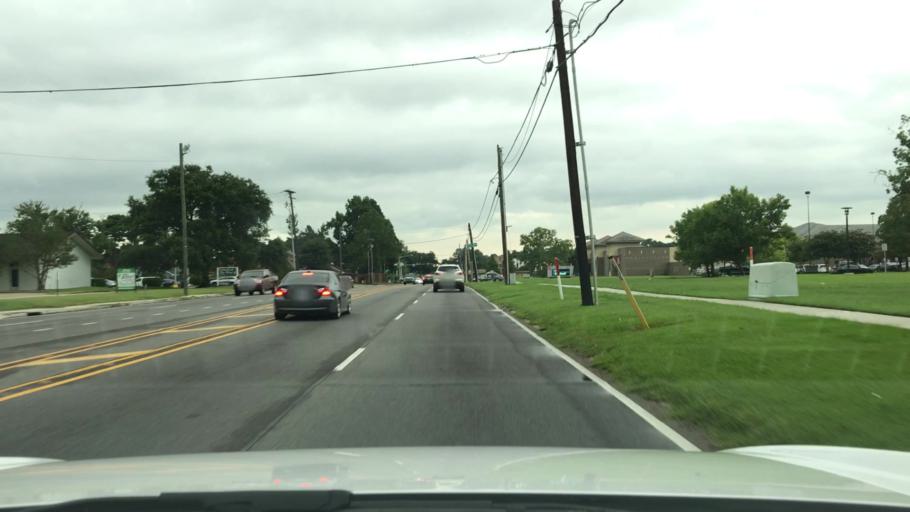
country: US
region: Louisiana
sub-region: East Baton Rouge Parish
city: Baton Rouge
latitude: 30.4461
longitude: -91.1387
